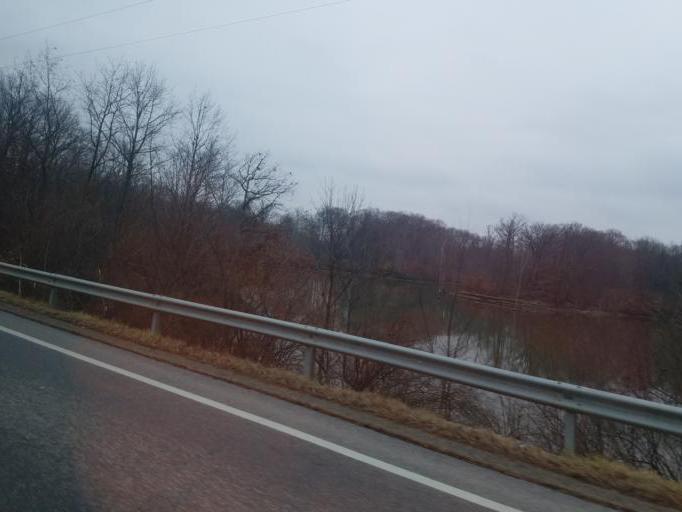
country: US
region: Ohio
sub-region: Delaware County
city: Lewis Center
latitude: 40.1976
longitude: -82.9442
